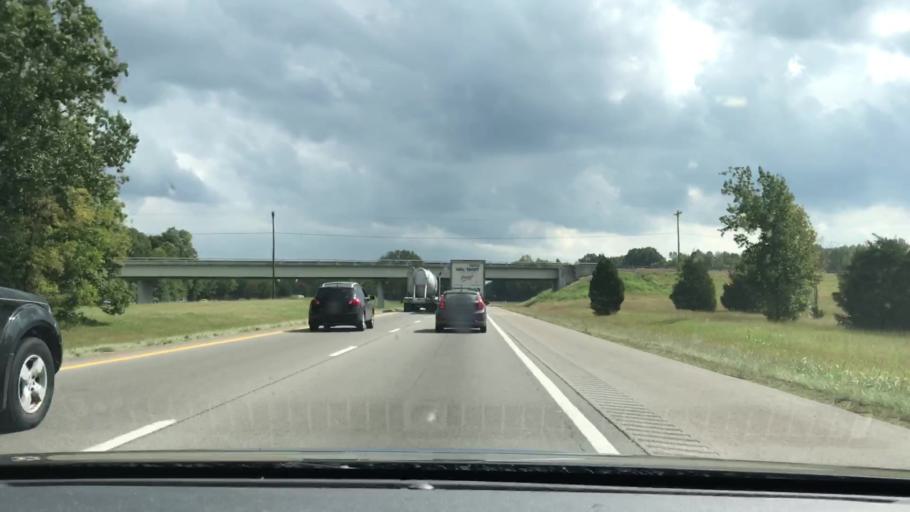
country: US
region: Tennessee
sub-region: Cheatham County
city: Pleasant View
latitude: 36.4508
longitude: -87.1010
